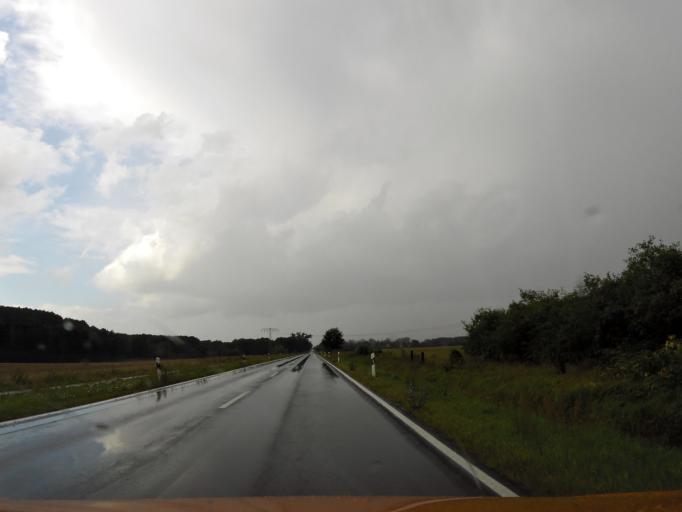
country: DE
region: Brandenburg
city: Wustermark
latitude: 52.4795
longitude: 12.9439
